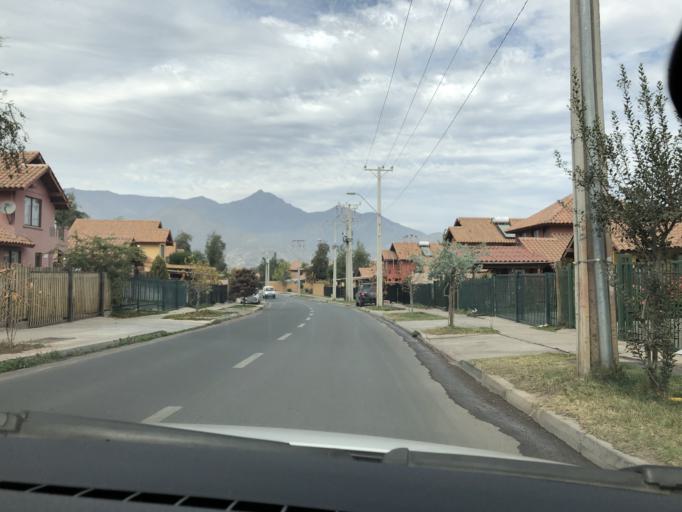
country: CL
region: Santiago Metropolitan
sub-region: Provincia de Cordillera
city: Puente Alto
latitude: -33.5850
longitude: -70.5138
